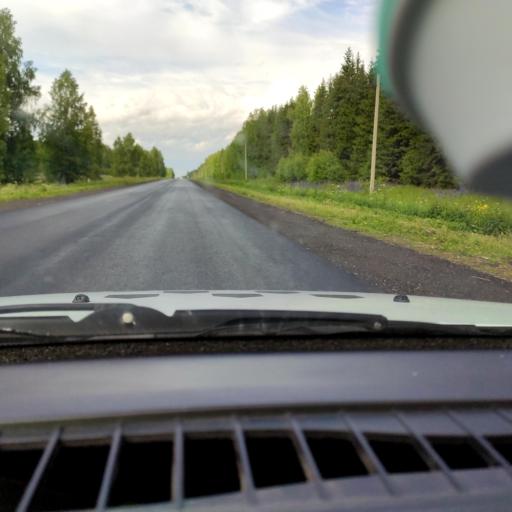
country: RU
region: Perm
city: Orda
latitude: 57.2269
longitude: 56.9616
